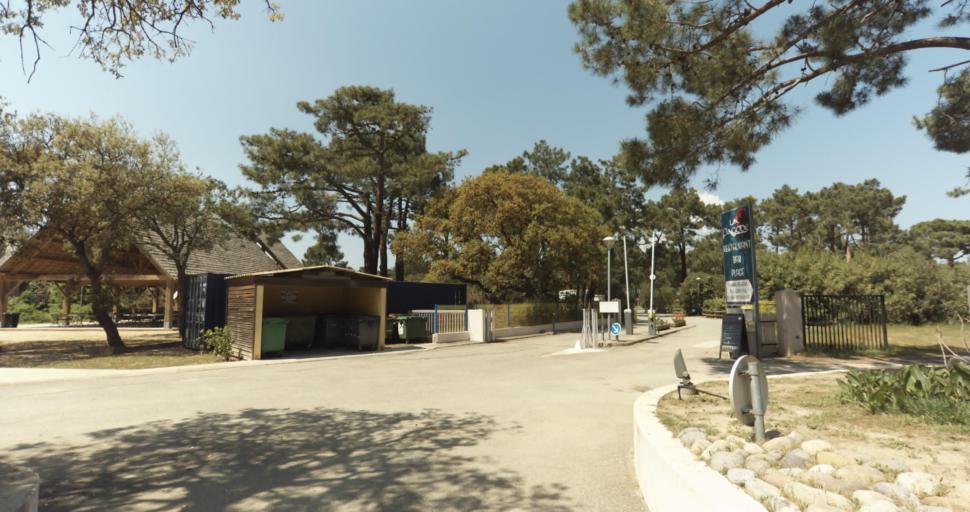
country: FR
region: Corsica
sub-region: Departement de la Haute-Corse
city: Biguglia
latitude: 42.6294
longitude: 9.4681
